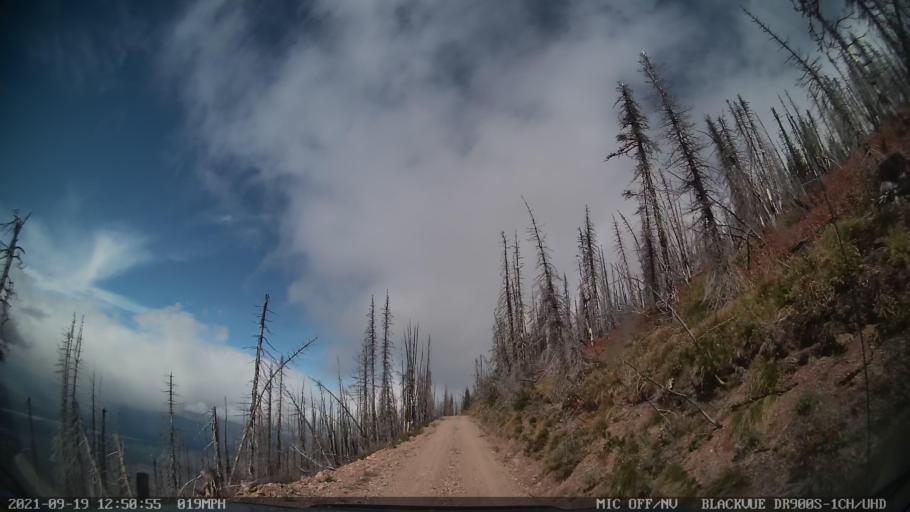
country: US
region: Montana
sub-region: Missoula County
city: Seeley Lake
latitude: 47.1875
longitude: -113.3585
